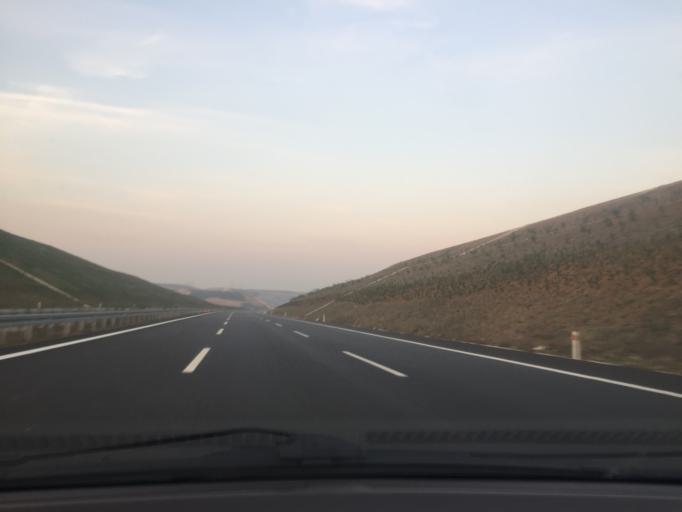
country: TR
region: Bursa
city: Mahmudiye
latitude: 40.2772
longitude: 28.5340
